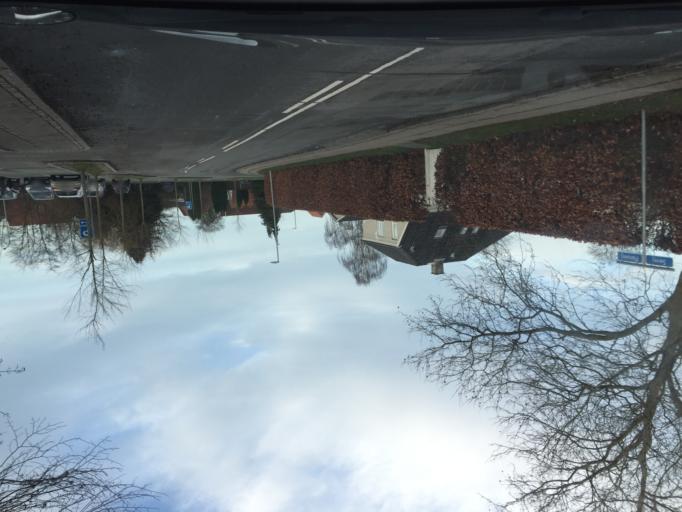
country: DK
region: South Denmark
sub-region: Faaborg-Midtfyn Kommune
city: Ringe
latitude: 55.2409
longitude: 10.4747
